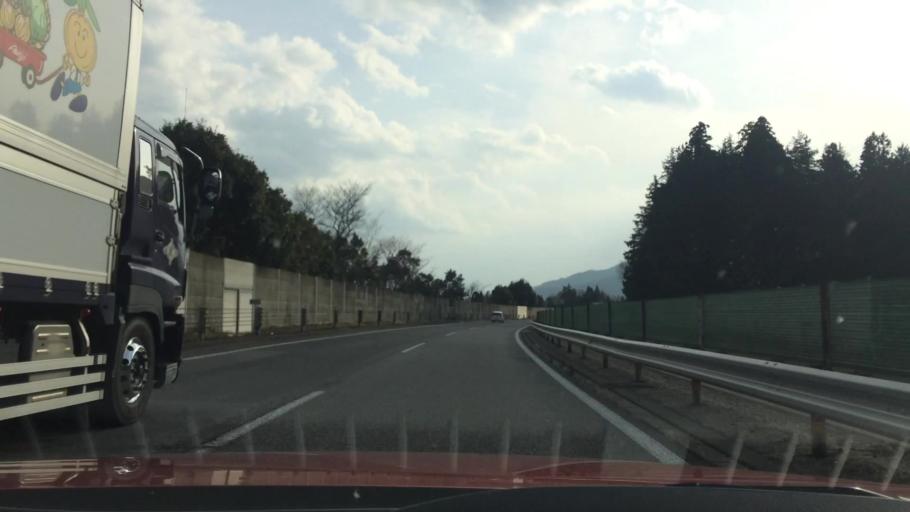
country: JP
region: Nagano
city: Ina
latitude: 35.8273
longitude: 137.9292
